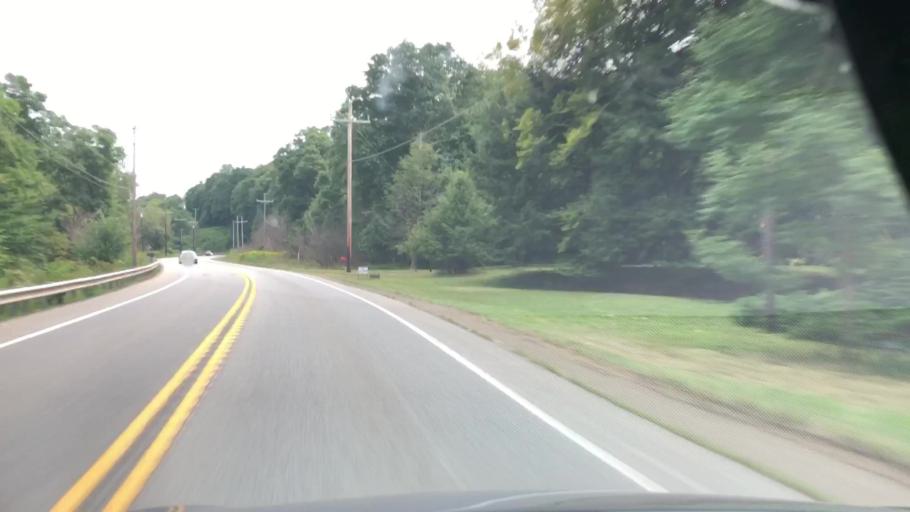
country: US
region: Pennsylvania
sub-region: Venango County
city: Hasson Heights
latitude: 41.4926
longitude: -79.7004
